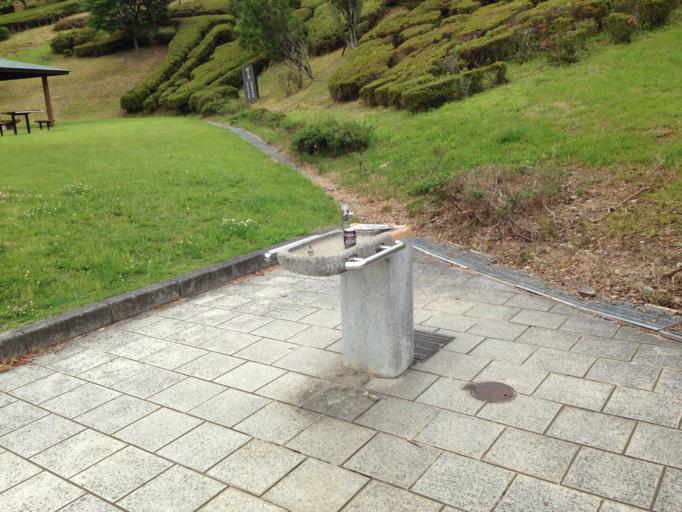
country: JP
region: Shizuoka
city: Fukuroi
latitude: 34.7441
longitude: 137.9420
